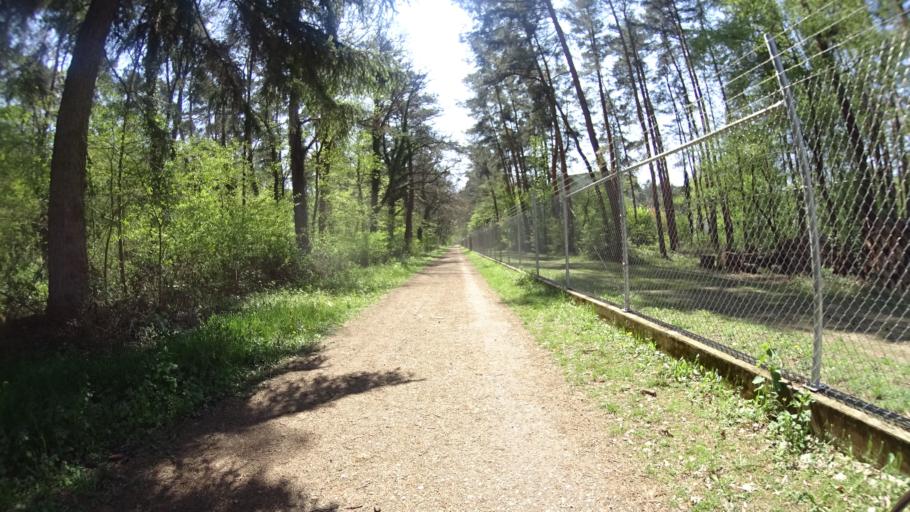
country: DE
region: Baden-Wuerttemberg
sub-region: Karlsruhe Region
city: Karlsruhe
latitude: 49.0443
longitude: 8.4044
